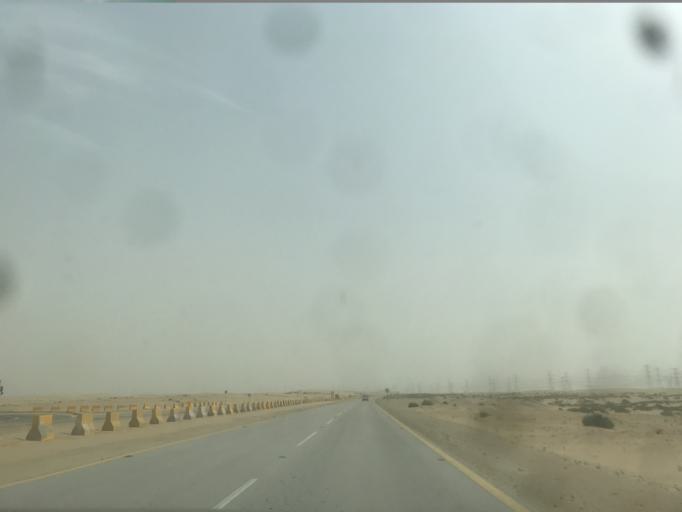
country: SA
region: Eastern Province
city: Abqaiq
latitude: 25.9145
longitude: 49.8711
